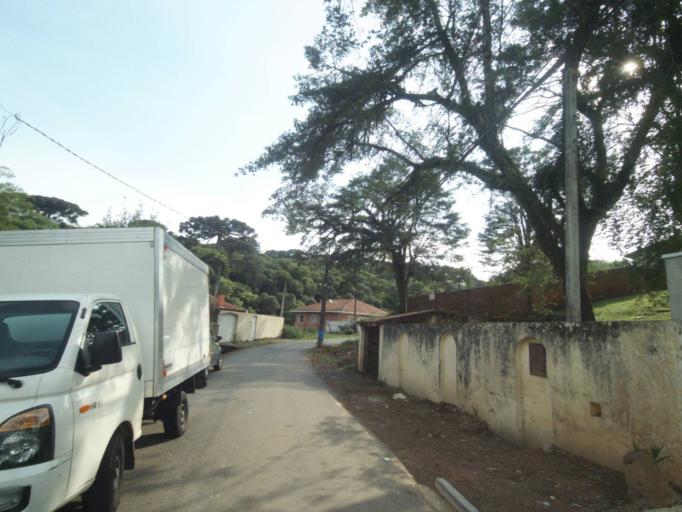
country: BR
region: Parana
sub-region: Curitiba
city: Curitiba
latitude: -25.4151
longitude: -49.3141
